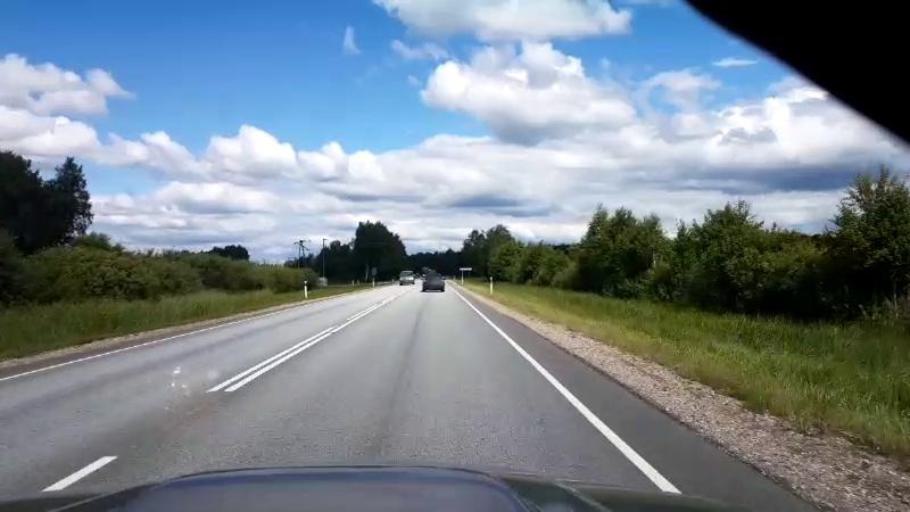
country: EE
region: Paernumaa
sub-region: Sauga vald
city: Sauga
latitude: 58.4540
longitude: 24.5088
